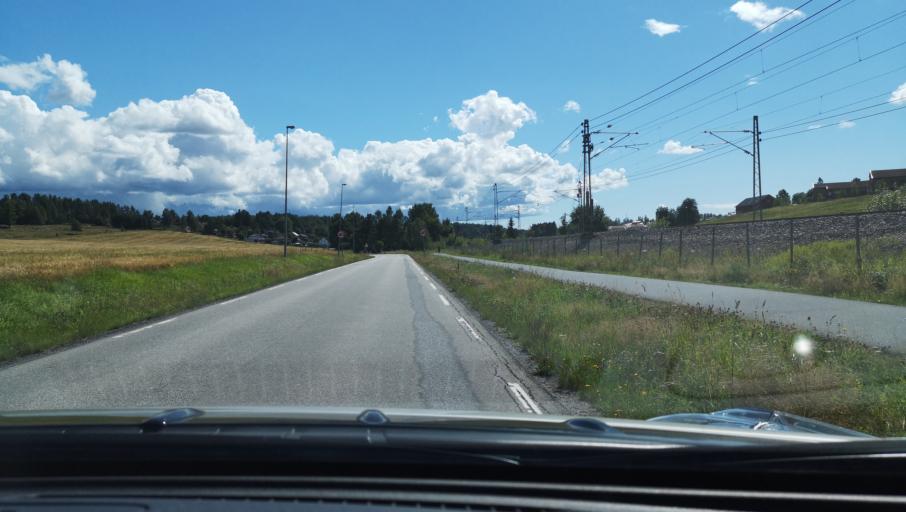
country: NO
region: Akershus
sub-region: As
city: As
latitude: 59.6599
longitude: 10.7968
